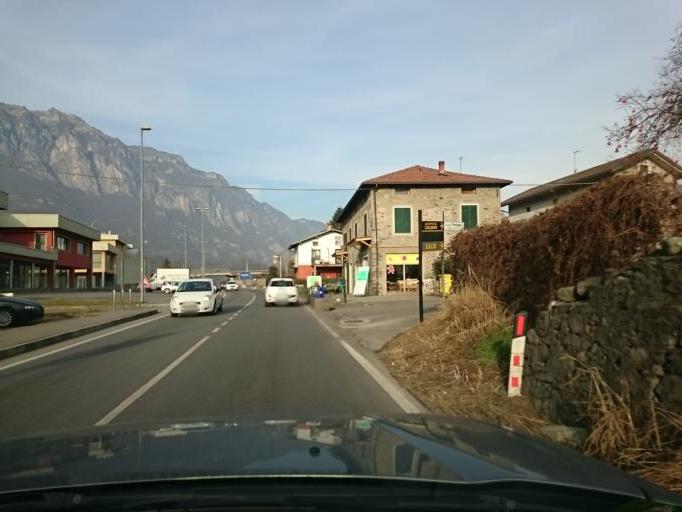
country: IT
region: Lombardy
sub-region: Provincia di Brescia
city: Gianico
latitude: 45.8695
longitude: 10.1705
